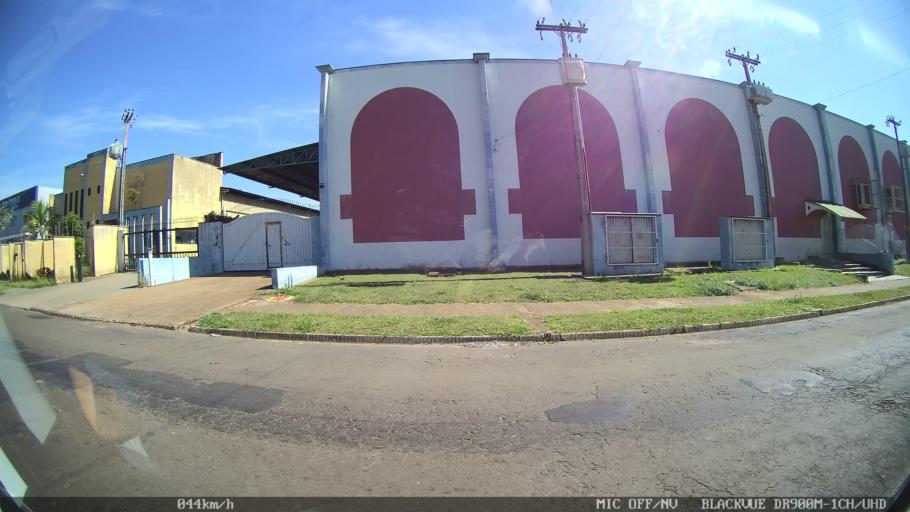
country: BR
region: Sao Paulo
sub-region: Franca
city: Franca
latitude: -20.5493
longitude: -47.4371
